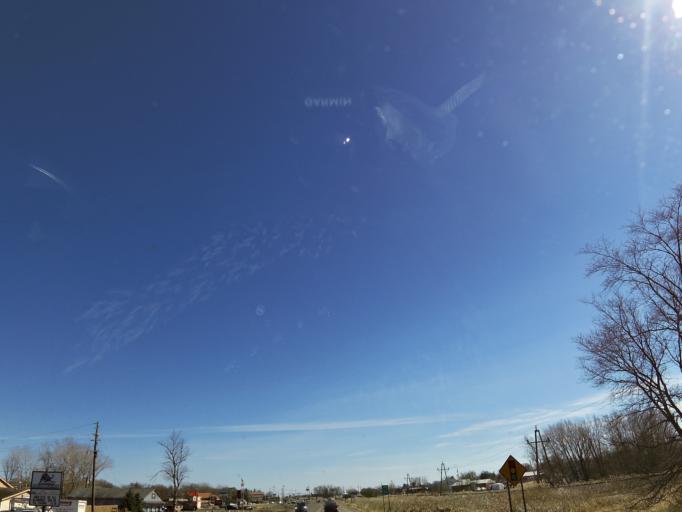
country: US
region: Minnesota
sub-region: Wright County
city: Buffalo
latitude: 45.1849
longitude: -93.8803
